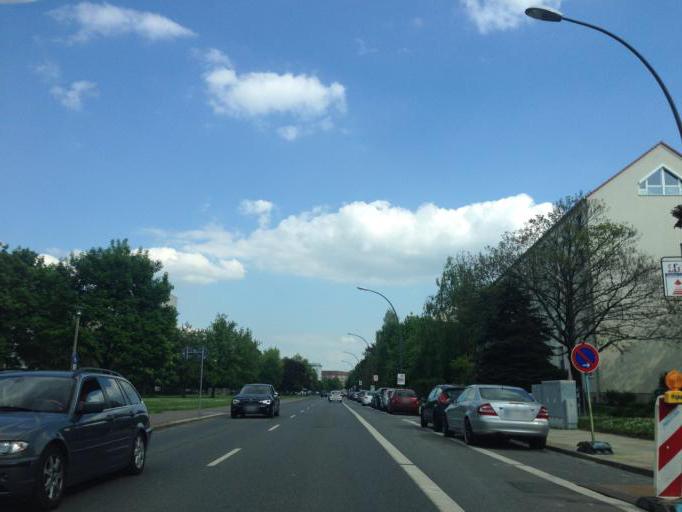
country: DE
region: Saxony
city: Dresden
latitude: 51.0489
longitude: 13.7624
